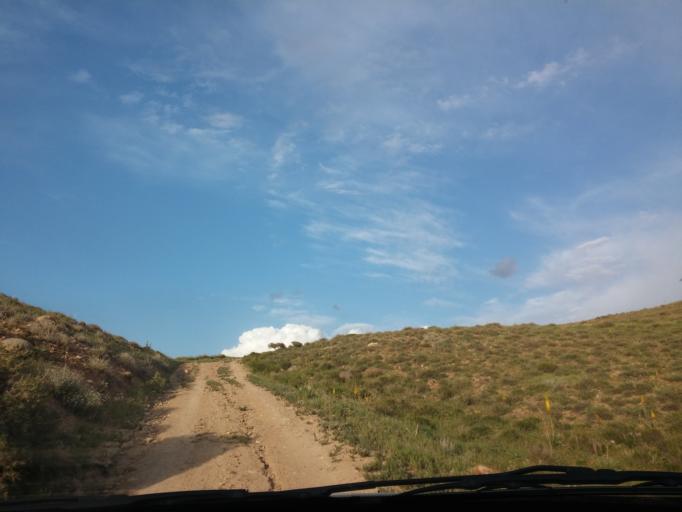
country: IR
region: Semnan
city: Istgah-e Rah Ahan-e Garmsar
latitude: 35.4904
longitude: 52.3054
